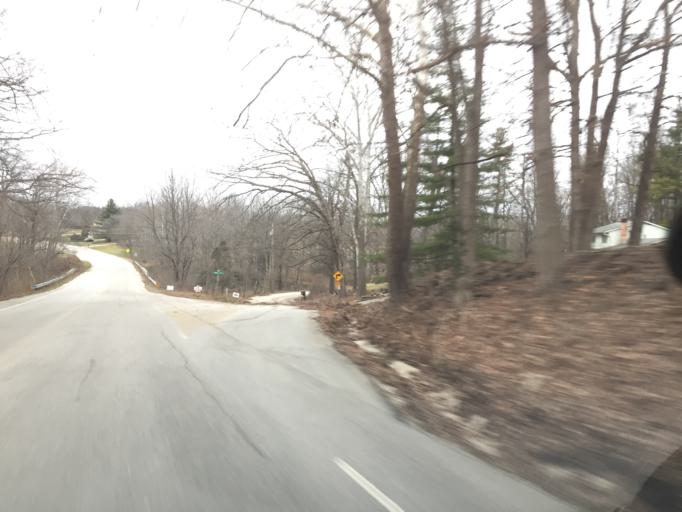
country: US
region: Indiana
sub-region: Monroe County
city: Bloomington
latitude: 39.1996
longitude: -86.5596
